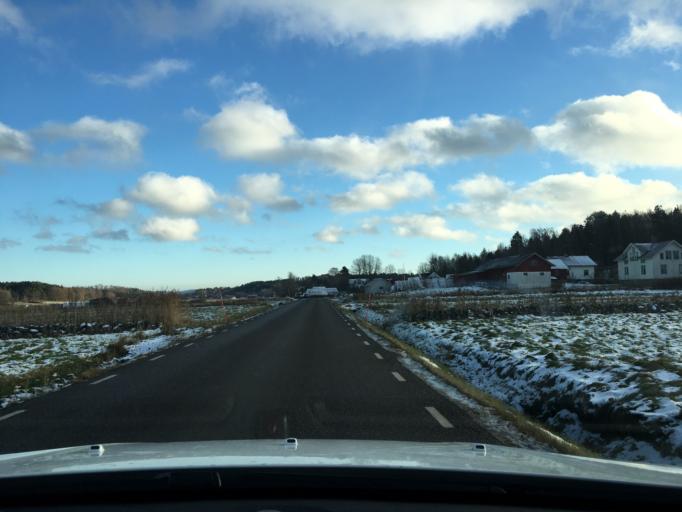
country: SE
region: Vaestra Goetaland
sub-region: Tjorns Kommun
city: Myggenas
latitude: 58.0477
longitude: 11.7208
